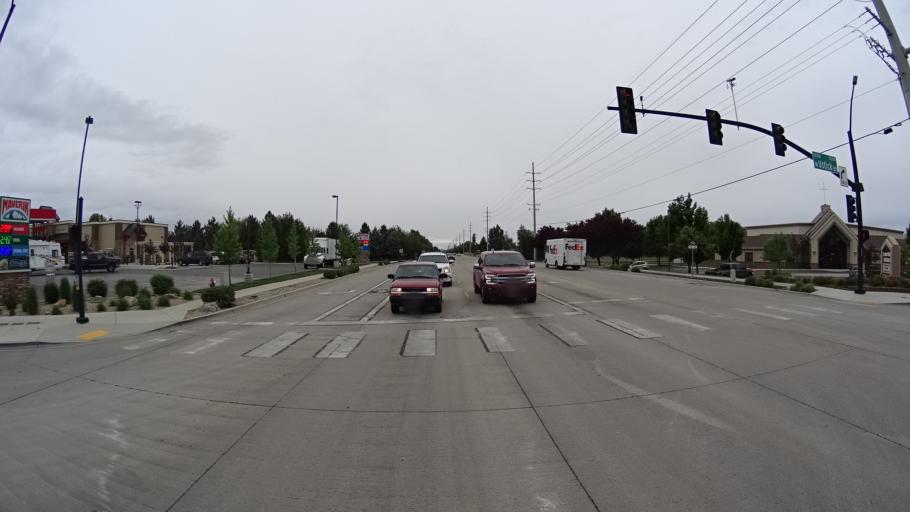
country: US
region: Idaho
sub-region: Ada County
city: Meridian
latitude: 43.6338
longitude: -116.3345
